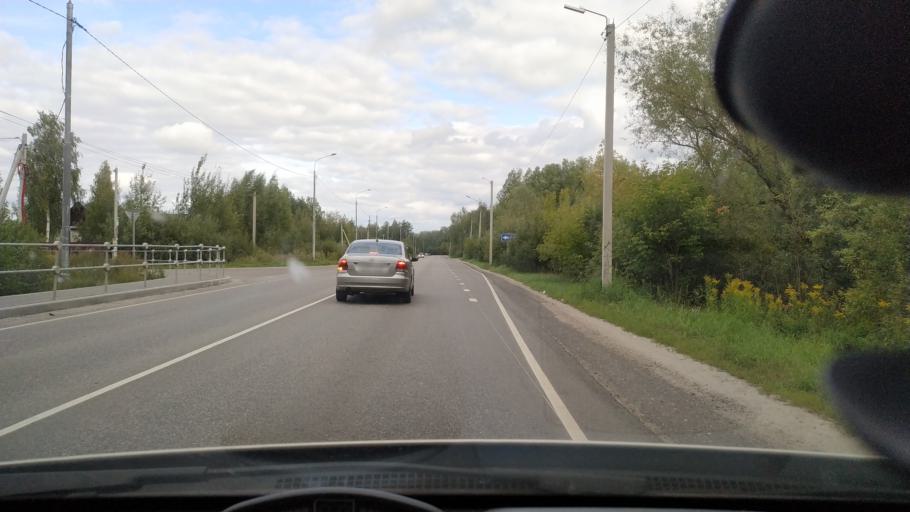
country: RU
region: Moskovskaya
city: Likino-Dulevo
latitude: 55.7266
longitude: 38.9718
